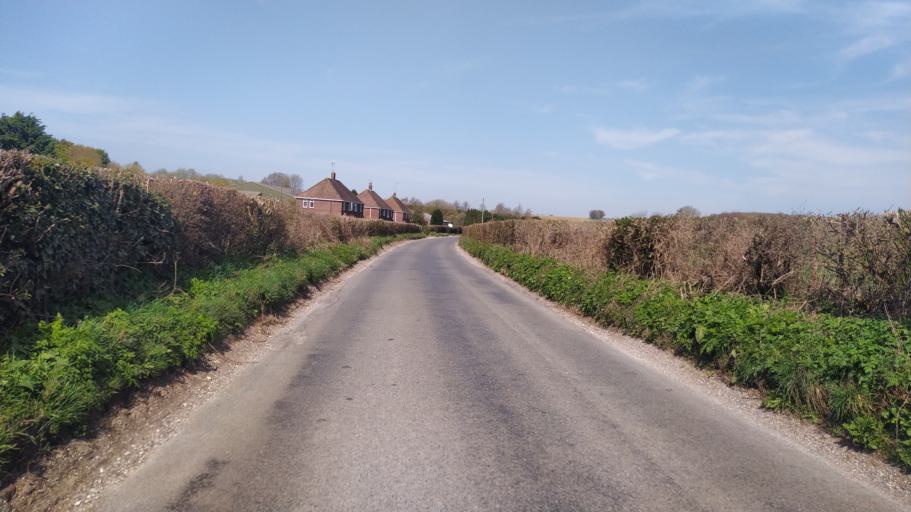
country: GB
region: England
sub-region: Hampshire
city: Four Marks
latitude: 51.0751
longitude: -1.1149
